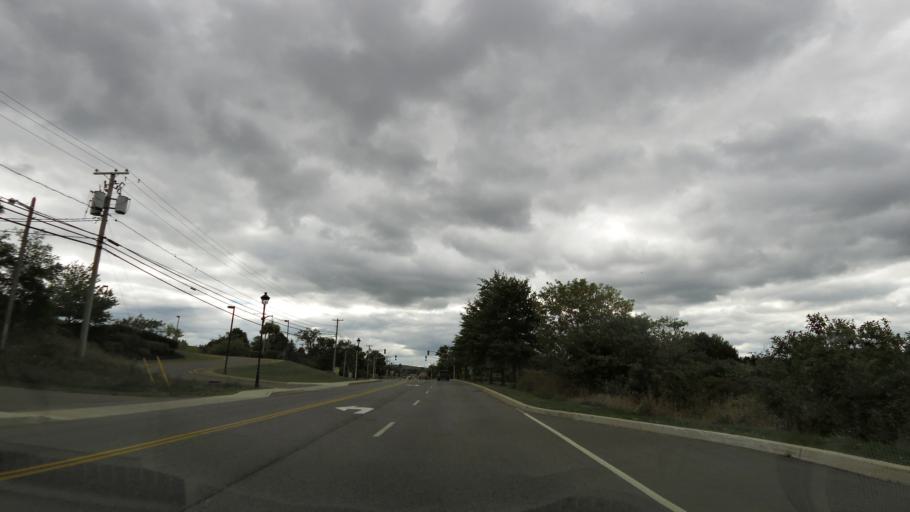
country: CA
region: New Brunswick
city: Hampton
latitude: 45.5223
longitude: -65.8311
